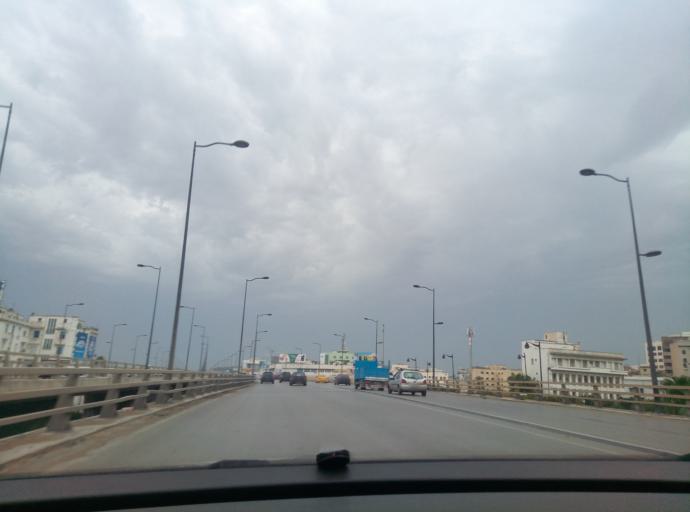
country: TN
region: Tunis
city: Tunis
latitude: 36.8013
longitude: 10.1887
